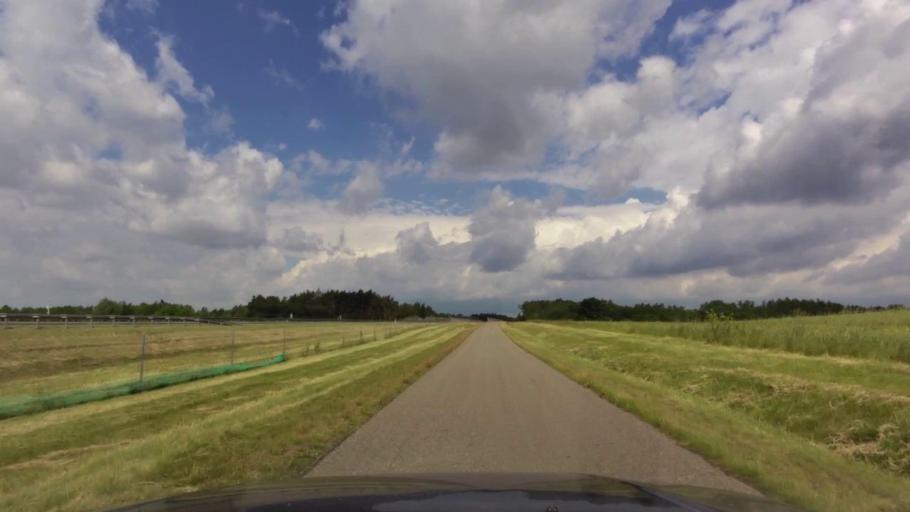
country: PL
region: West Pomeranian Voivodeship
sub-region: Powiat pyrzycki
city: Lipiany
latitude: 52.9606
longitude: 14.9272
